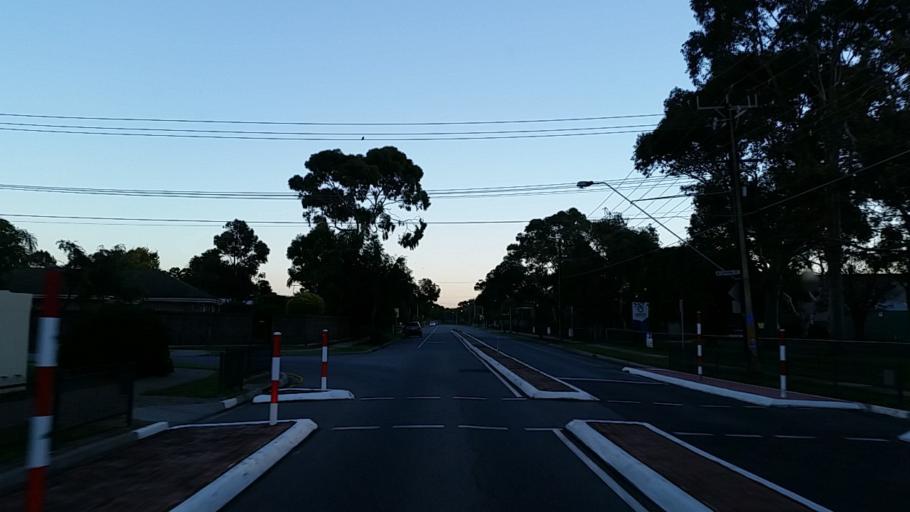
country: AU
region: South Australia
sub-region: Charles Sturt
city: Henley Beach
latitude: -34.9203
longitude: 138.5043
